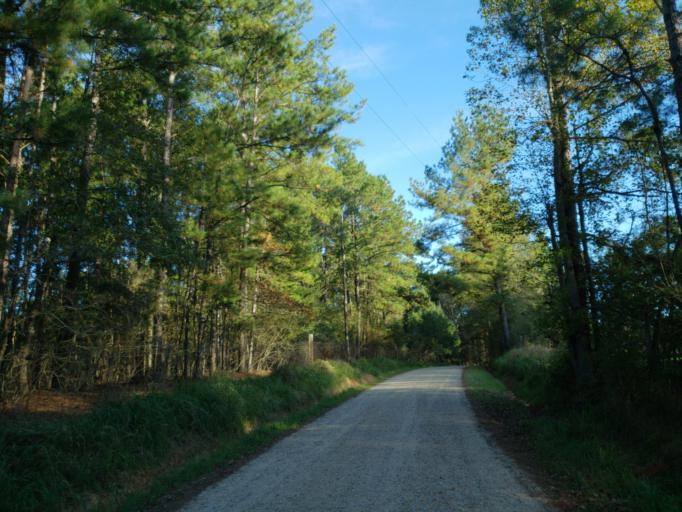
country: US
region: Mississippi
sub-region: Perry County
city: Richton
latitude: 31.3523
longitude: -88.8064
